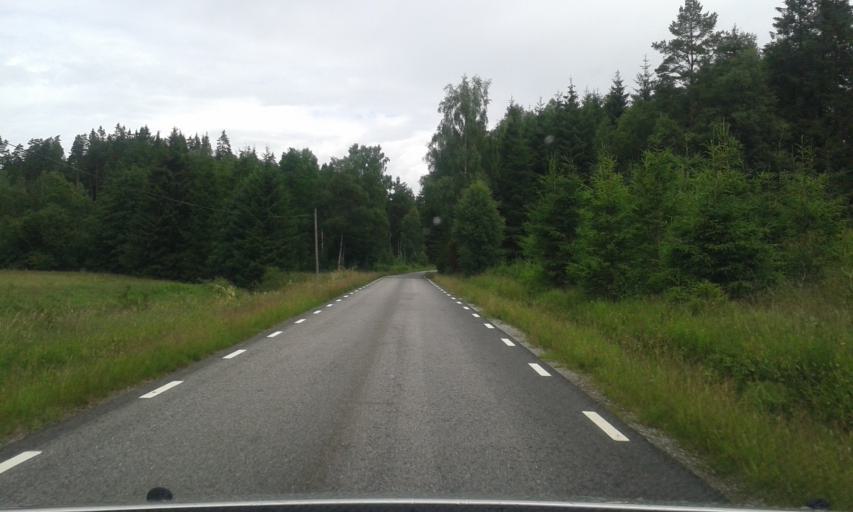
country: SE
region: Vaestra Goetaland
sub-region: Kungalvs Kommun
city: Diserod
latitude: 57.9688
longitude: 11.9673
